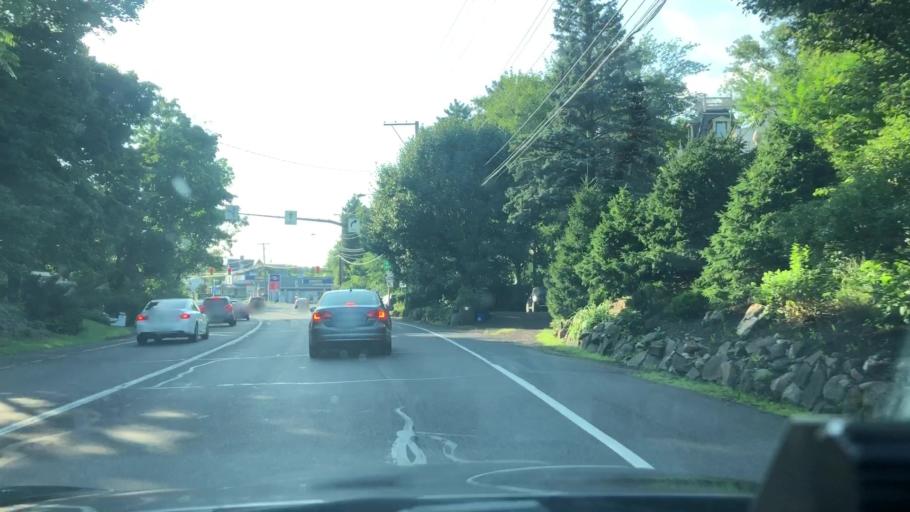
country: US
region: Pennsylvania
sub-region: Lehigh County
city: Coopersburg
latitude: 40.5286
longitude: -75.3924
